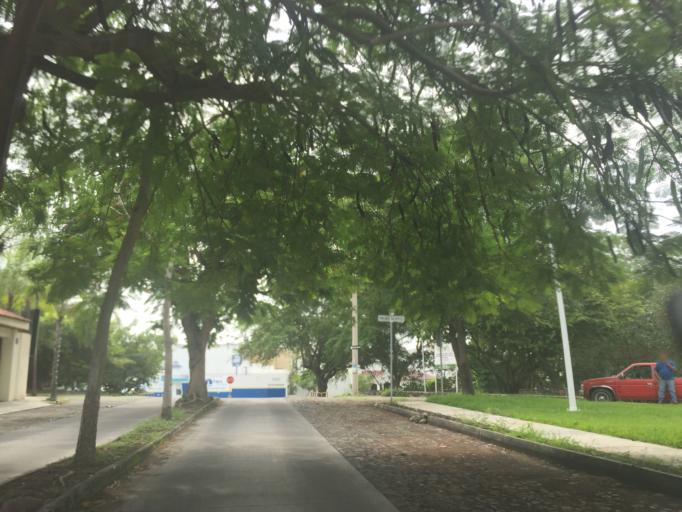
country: MX
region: Colima
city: Colima
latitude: 19.2621
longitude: -103.7148
